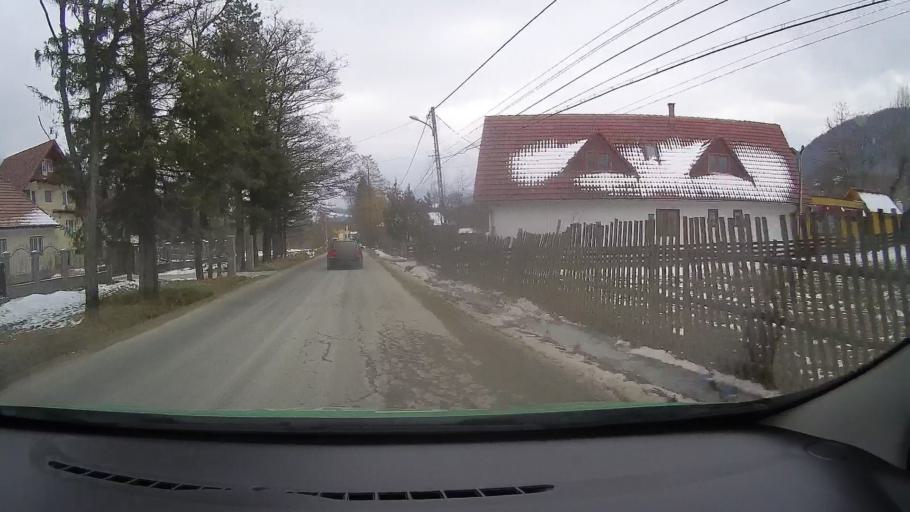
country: RO
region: Brasov
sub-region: Comuna Bran
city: Bran
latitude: 45.5301
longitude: 25.3538
